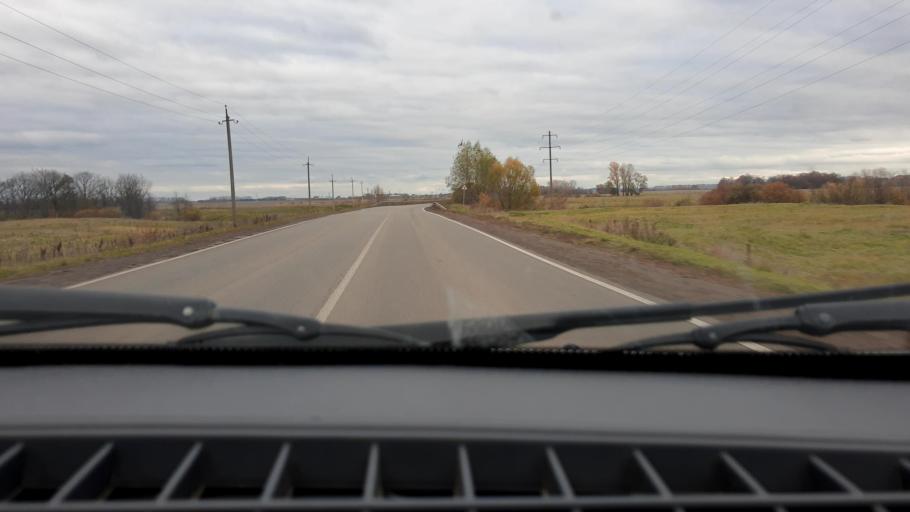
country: RU
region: Bashkortostan
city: Kabakovo
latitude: 54.5637
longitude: 55.9955
